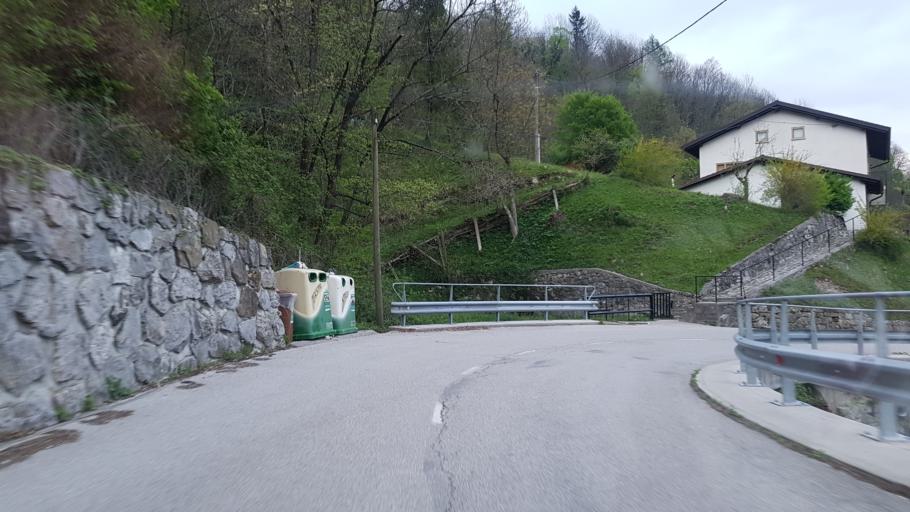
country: SI
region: Kobarid
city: Kobarid
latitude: 46.2536
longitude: 13.5069
